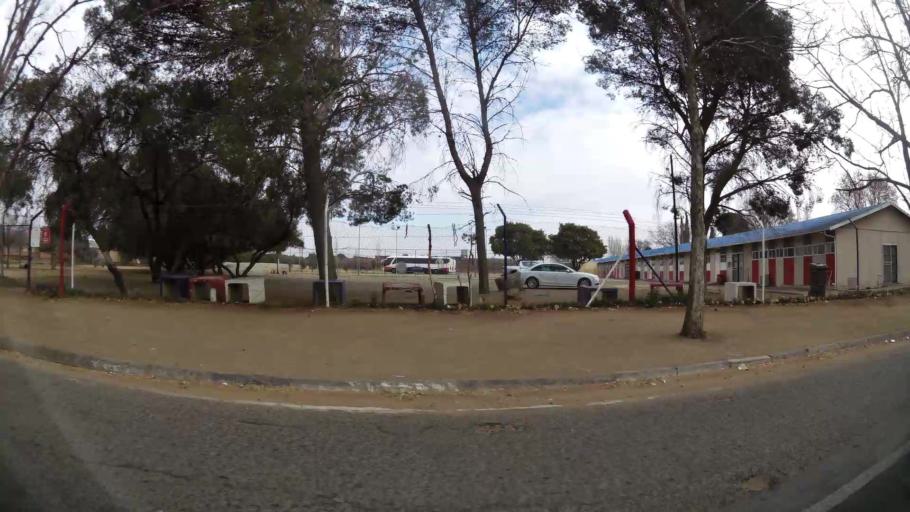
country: ZA
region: Orange Free State
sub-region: Mangaung Metropolitan Municipality
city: Bloemfontein
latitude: -29.1314
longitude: 26.2069
